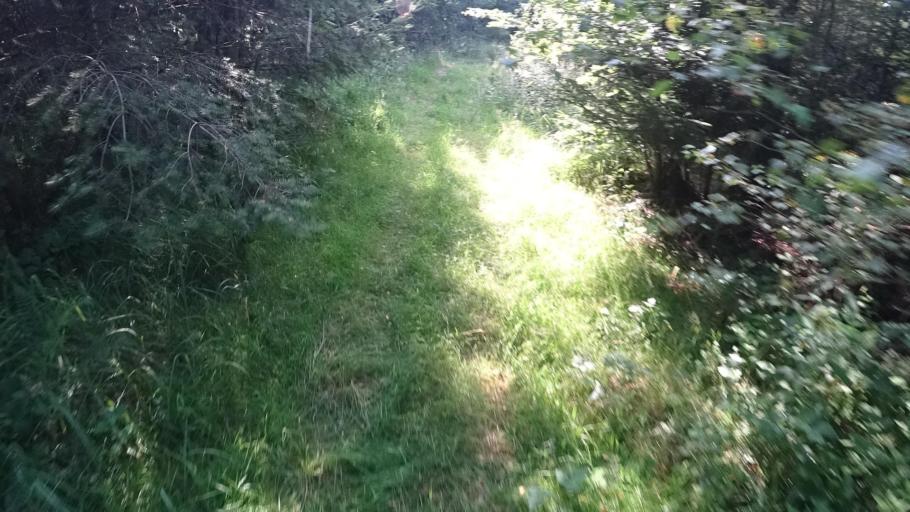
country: DE
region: Rheinland-Pfalz
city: Sankt Katharinen
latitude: 50.5687
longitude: 7.3761
